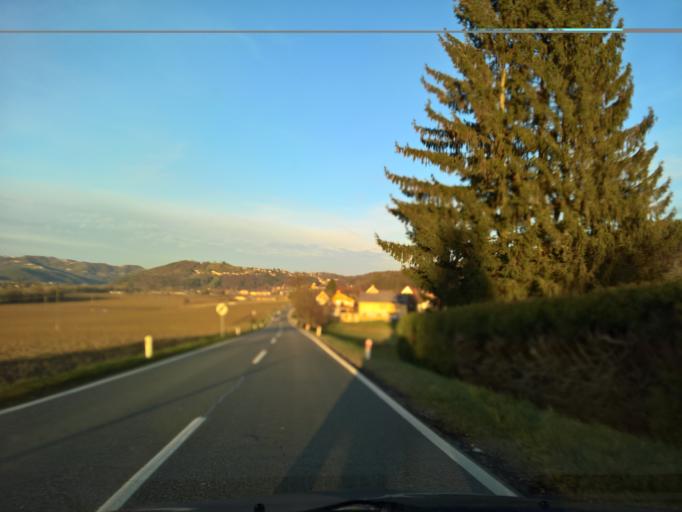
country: AT
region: Styria
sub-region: Politischer Bezirk Leibnitz
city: Grossklein
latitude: 46.7251
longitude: 15.4224
